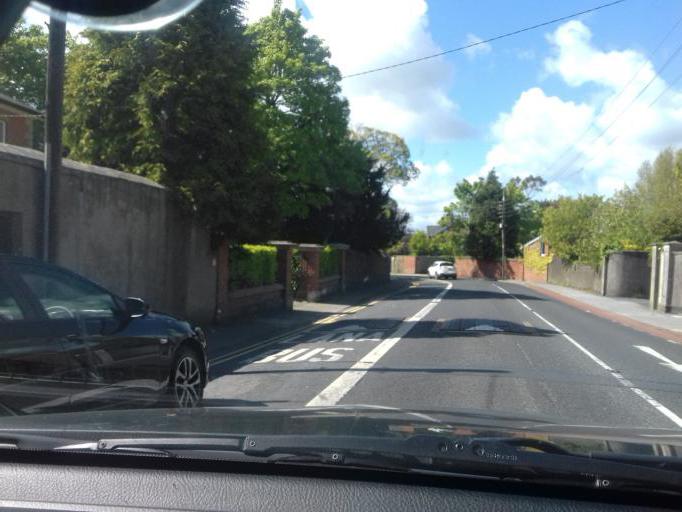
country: IE
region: Munster
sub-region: Waterford
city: Waterford
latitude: 52.2514
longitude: -7.0964
